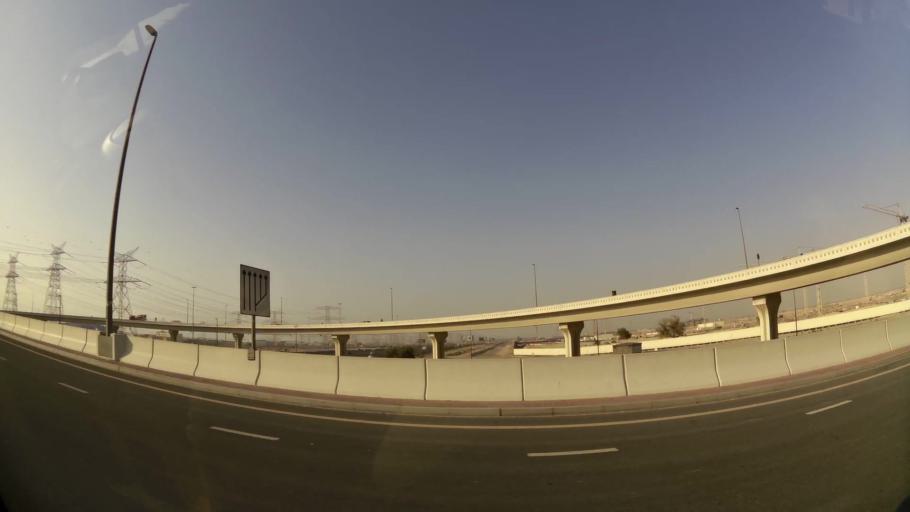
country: AE
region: Dubai
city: Dubai
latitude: 25.1015
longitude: 55.2339
